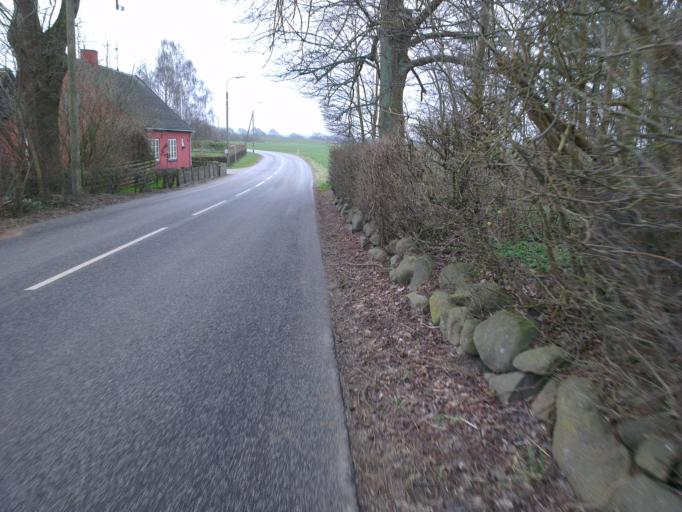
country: DK
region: Capital Region
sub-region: Frederikssund Kommune
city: Skibby
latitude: 55.7496
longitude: 11.9206
